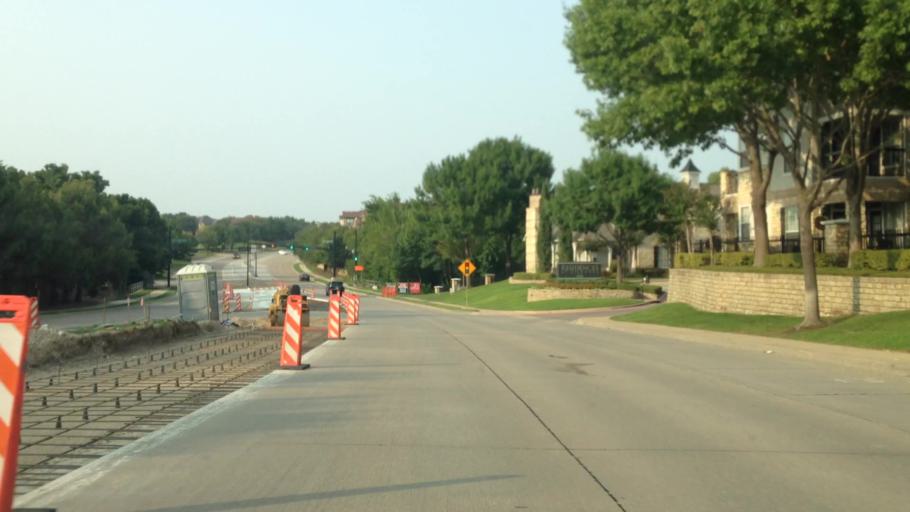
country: US
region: Texas
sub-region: Collin County
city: Frisco
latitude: 33.1188
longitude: -96.8282
